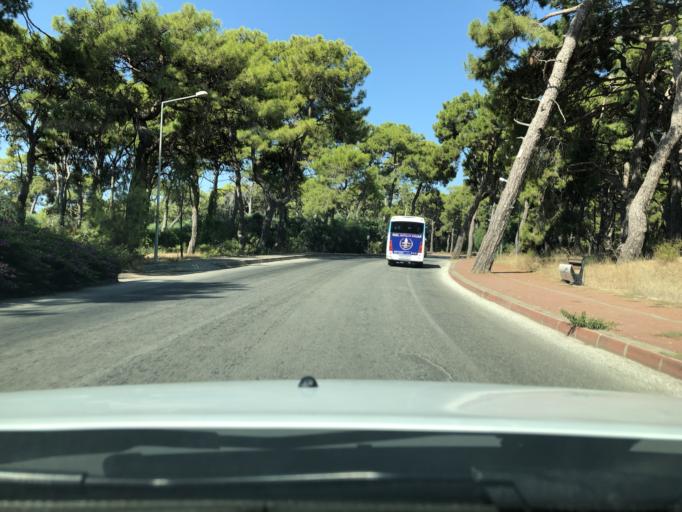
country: TR
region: Antalya
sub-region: Manavgat
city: Manavgat
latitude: 36.7591
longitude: 31.4313
